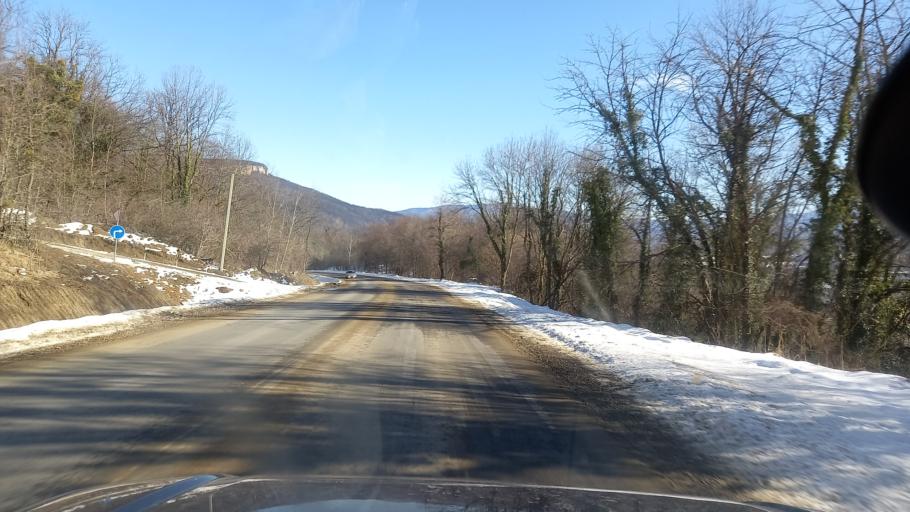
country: RU
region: Adygeya
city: Kamennomostskiy
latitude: 44.2397
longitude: 40.1741
